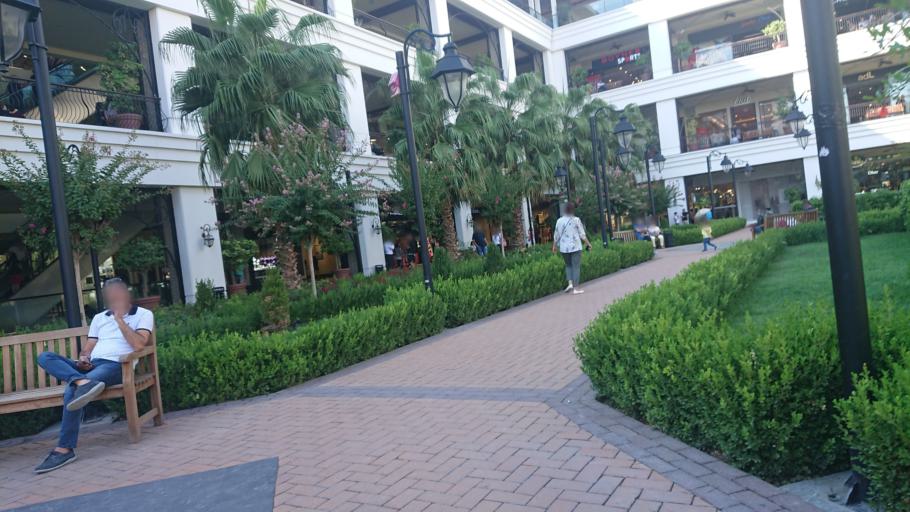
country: TR
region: Izmir
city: Karsiyaka
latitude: 38.4740
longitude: 27.0746
